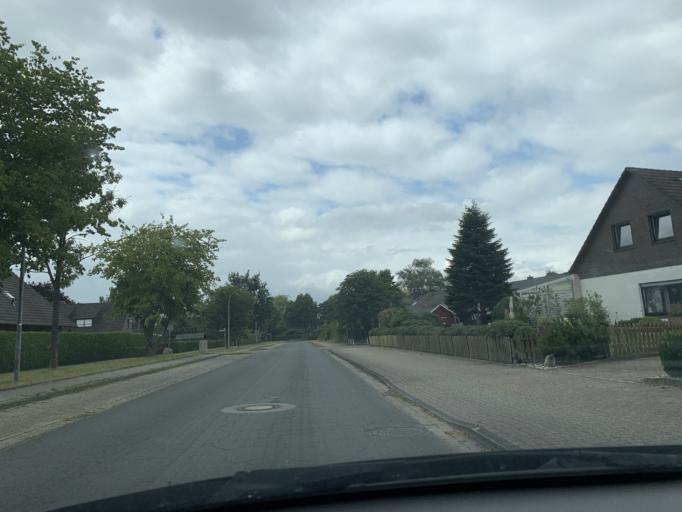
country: DE
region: Lower Saxony
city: Westerstede
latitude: 53.2538
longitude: 7.9473
